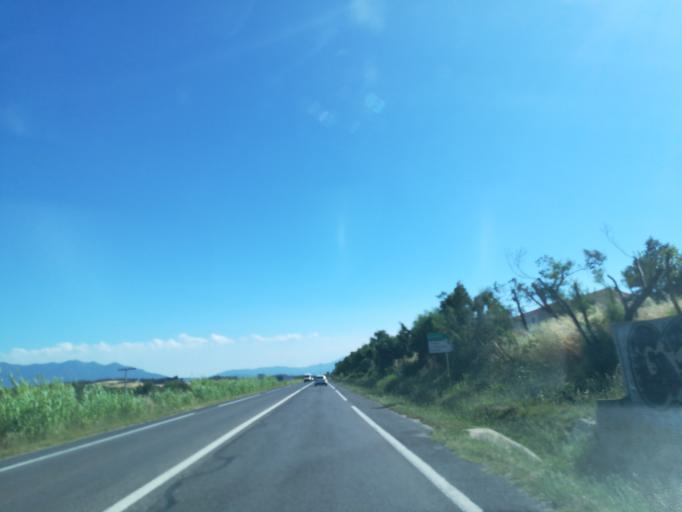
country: FR
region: Languedoc-Roussillon
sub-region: Departement des Pyrenees-Orientales
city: Pollestres
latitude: 42.6355
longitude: 2.8731
